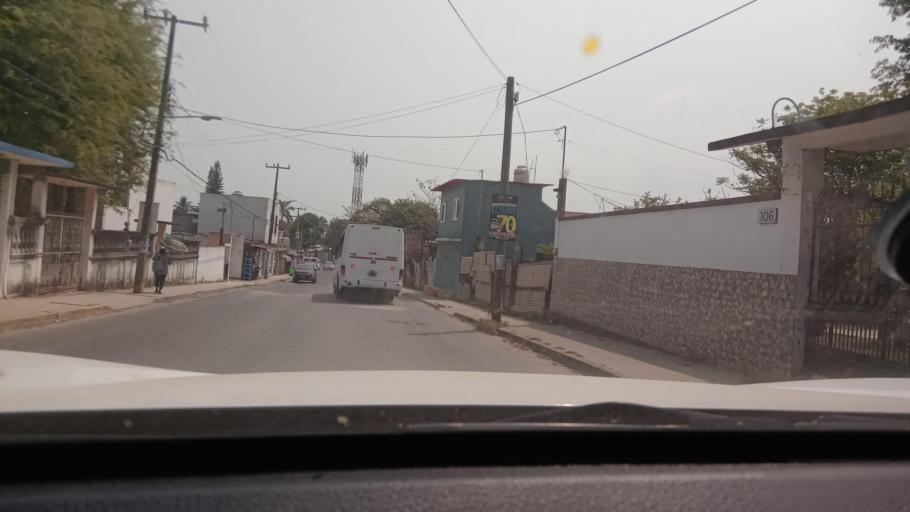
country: MX
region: Veracruz
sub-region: Minatitlan
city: Las Lomas
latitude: 17.9774
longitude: -94.5697
